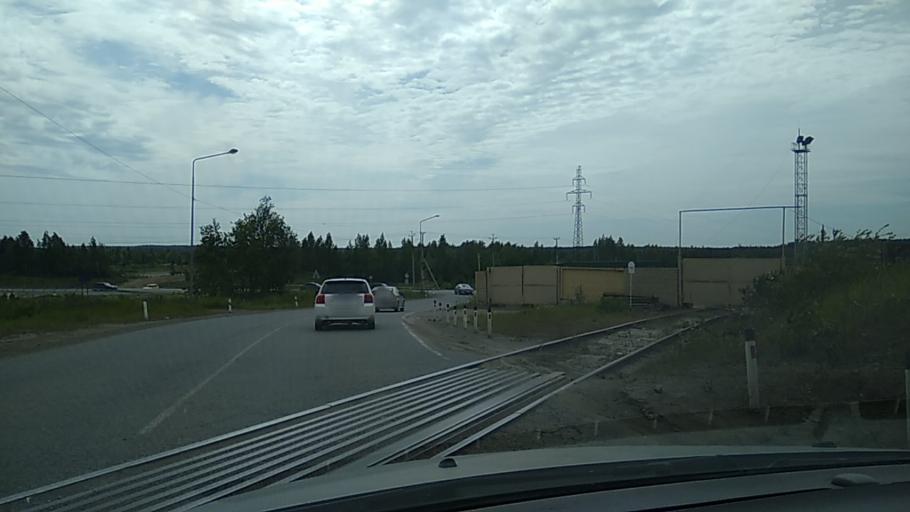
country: RU
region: Sverdlovsk
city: Verkhnyaya Pyshma
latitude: 56.9535
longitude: 60.5861
